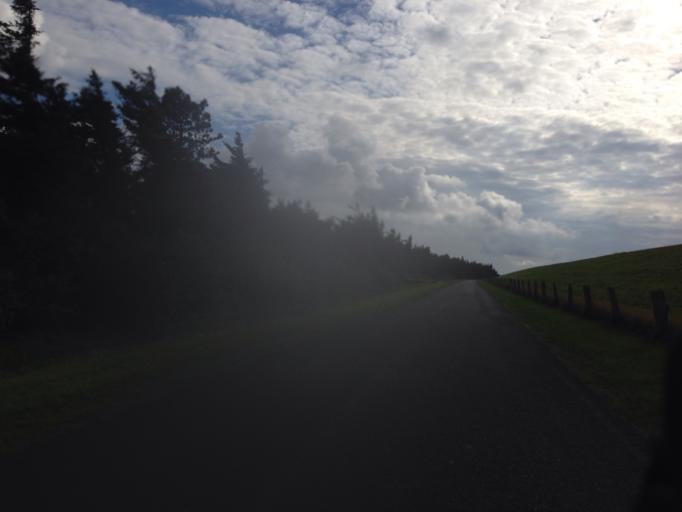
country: DE
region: Schleswig-Holstein
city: Utersum
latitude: 54.7246
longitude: 8.4025
